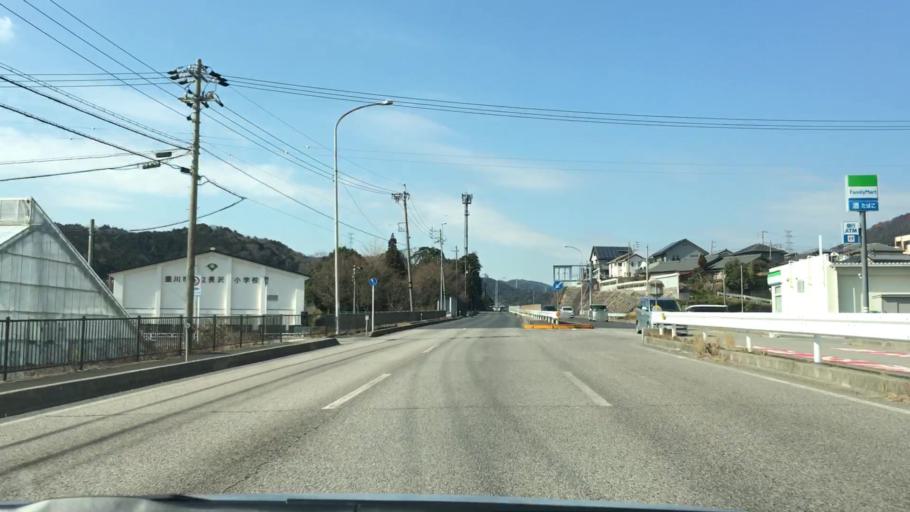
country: JP
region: Aichi
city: Gamagori
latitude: 34.8682
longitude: 137.2925
